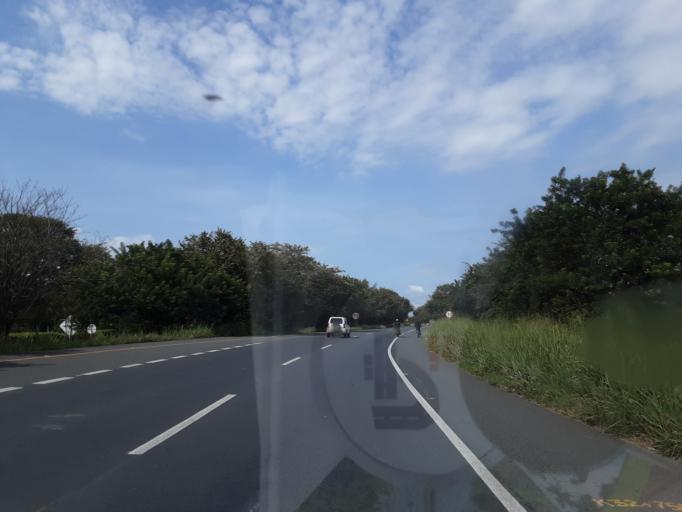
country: CO
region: Valle del Cauca
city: Guacari
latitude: 3.8212
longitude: -76.3055
